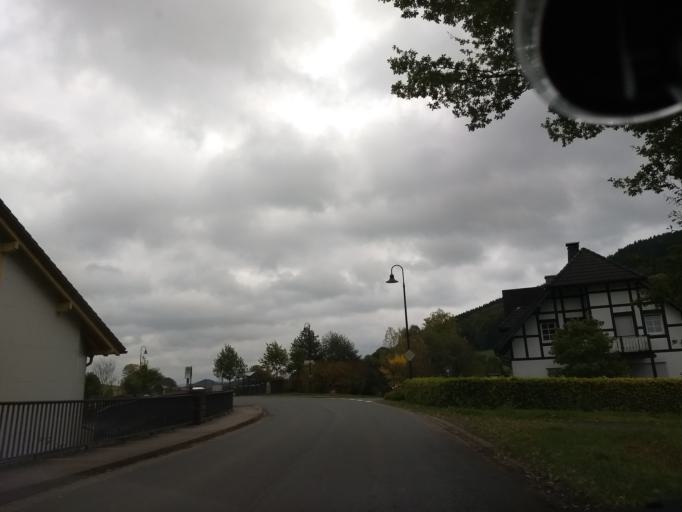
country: DE
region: North Rhine-Westphalia
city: Eslohe
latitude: 51.2491
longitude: 8.0998
